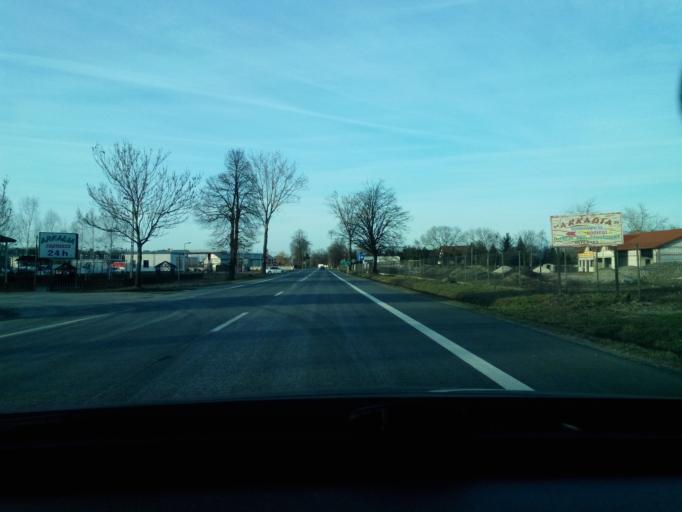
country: PL
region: Kujawsko-Pomorskie
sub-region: Powiat wloclawski
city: Lubien Kujawski
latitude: 52.3954
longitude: 19.1711
